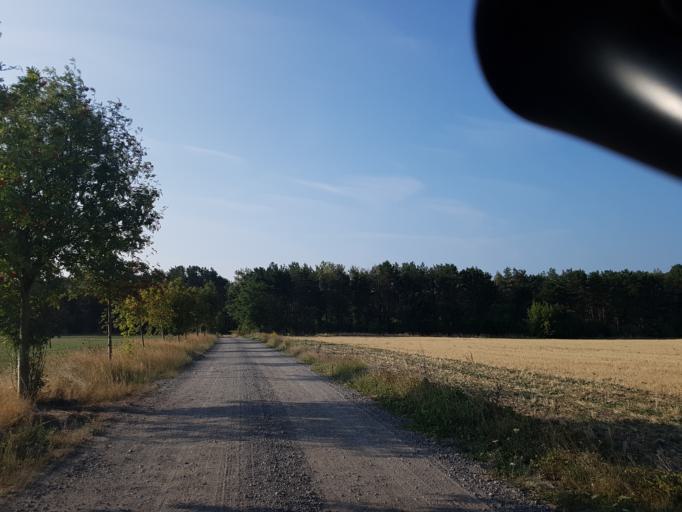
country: DE
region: Brandenburg
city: Niemegk
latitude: 52.0772
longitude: 12.7159
